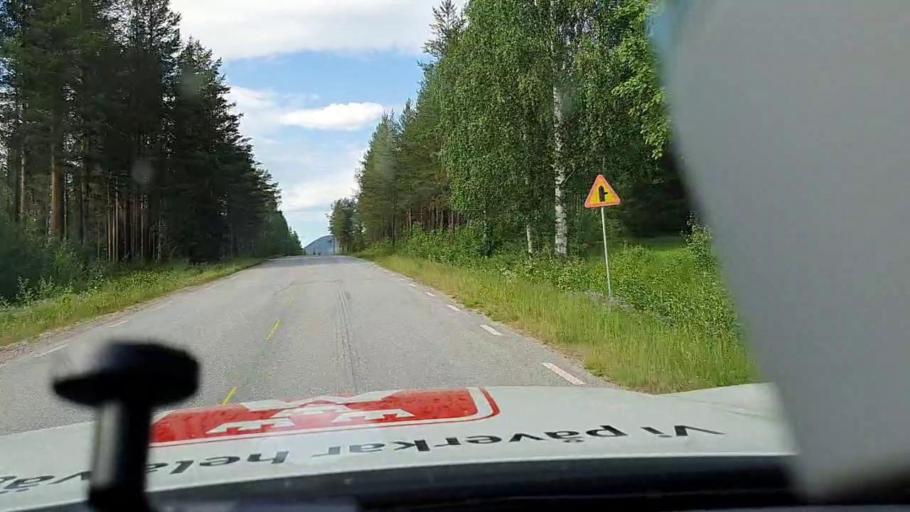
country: SE
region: Norrbotten
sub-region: Gallivare Kommun
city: Gaellivare
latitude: 66.4559
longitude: 20.6559
